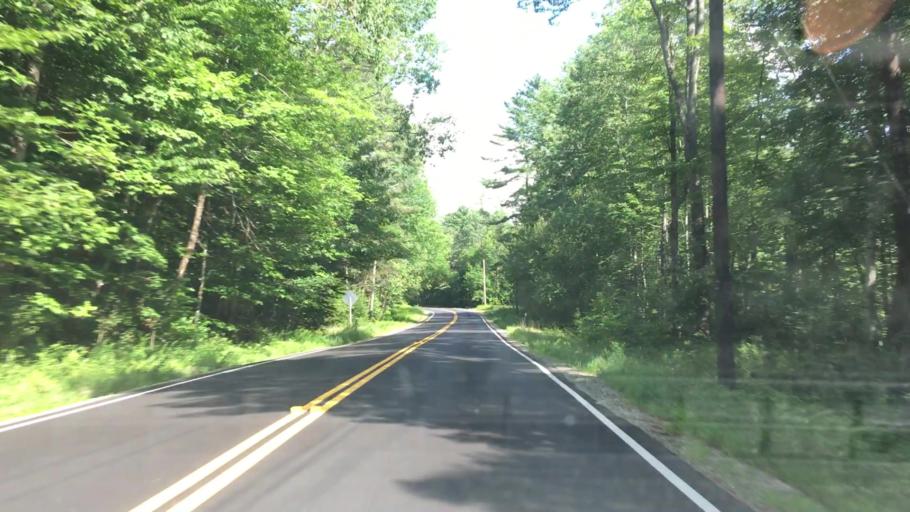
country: US
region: New Hampshire
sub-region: Grafton County
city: North Haverhill
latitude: 44.1059
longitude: -71.8736
